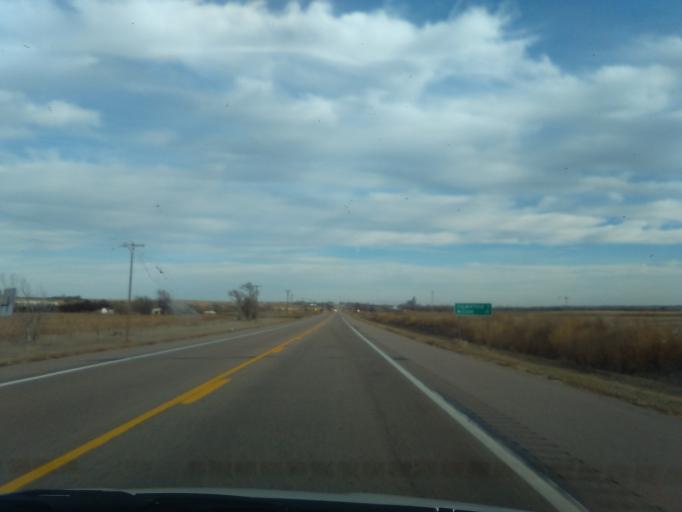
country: US
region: Nebraska
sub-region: Hitchcock County
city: Trenton
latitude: 40.2343
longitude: -100.8942
